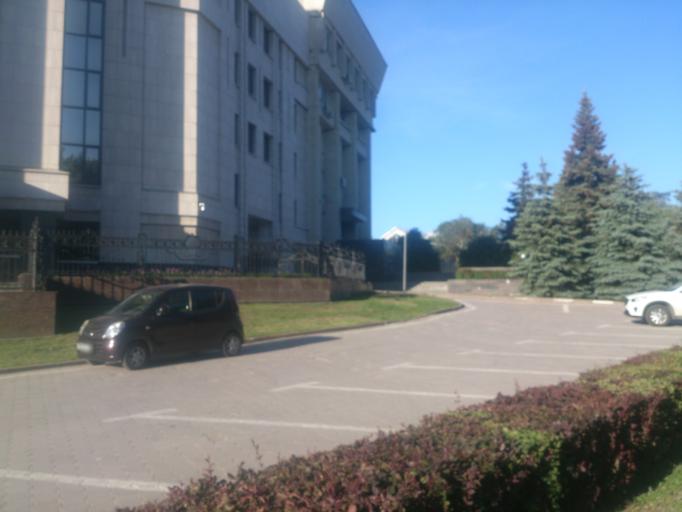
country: RU
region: Ulyanovsk
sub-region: Ulyanovskiy Rayon
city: Ulyanovsk
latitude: 54.3217
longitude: 48.4032
